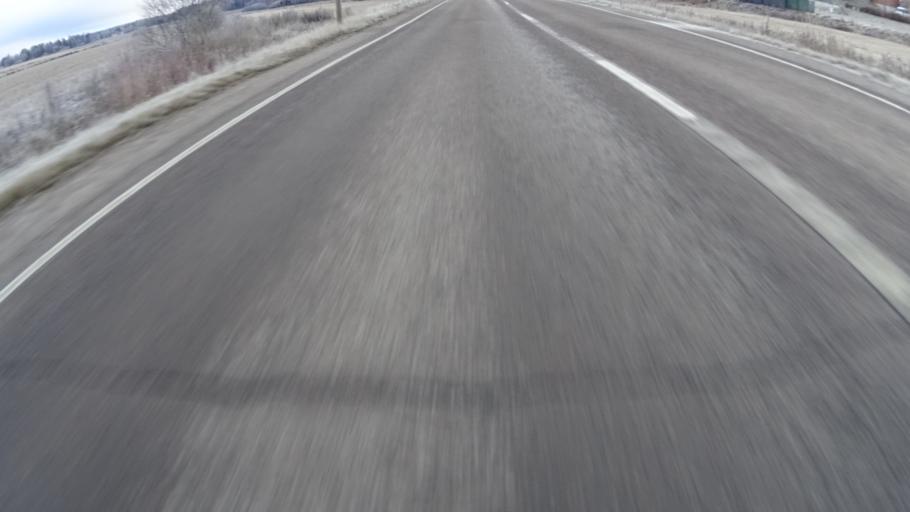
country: FI
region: Uusimaa
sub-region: Helsinki
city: Nurmijaervi
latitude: 60.4365
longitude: 24.7097
